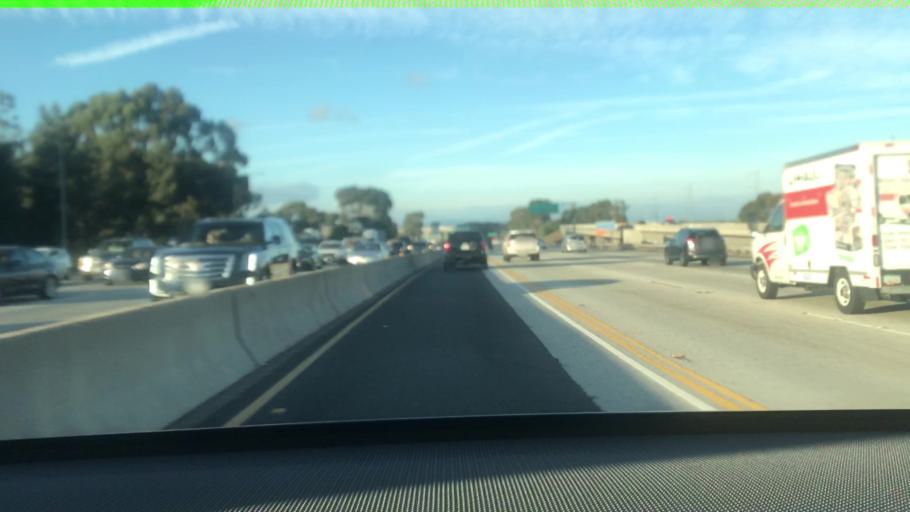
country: US
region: California
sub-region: Los Angeles County
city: Del Aire
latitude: 33.9167
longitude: -118.3702
